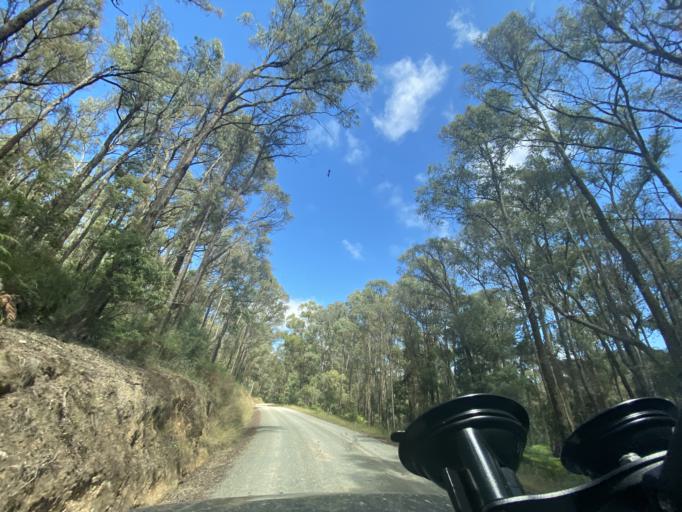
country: AU
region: Victoria
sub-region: Yarra Ranges
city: Millgrove
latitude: -37.5189
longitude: 146.0359
